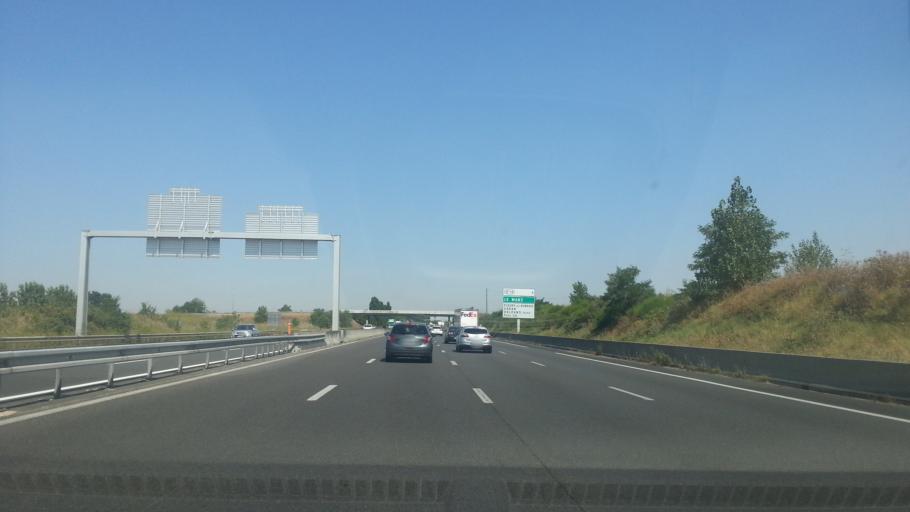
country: FR
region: Centre
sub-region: Departement du Loiret
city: Saint-Jean-de-la-Ruelle
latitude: 47.9122
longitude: 1.8494
